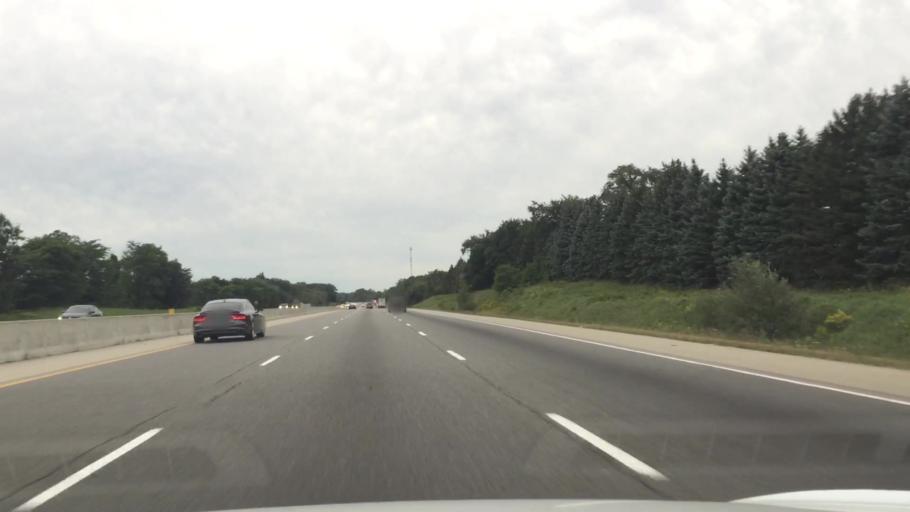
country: CA
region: Ontario
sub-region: Oxford County
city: Woodstock
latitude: 43.2104
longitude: -80.6135
